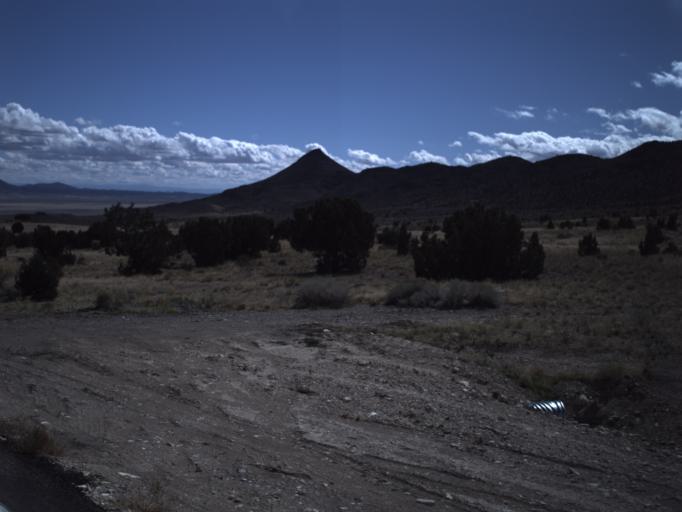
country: US
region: Utah
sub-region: Beaver County
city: Milford
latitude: 38.5067
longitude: -113.5152
